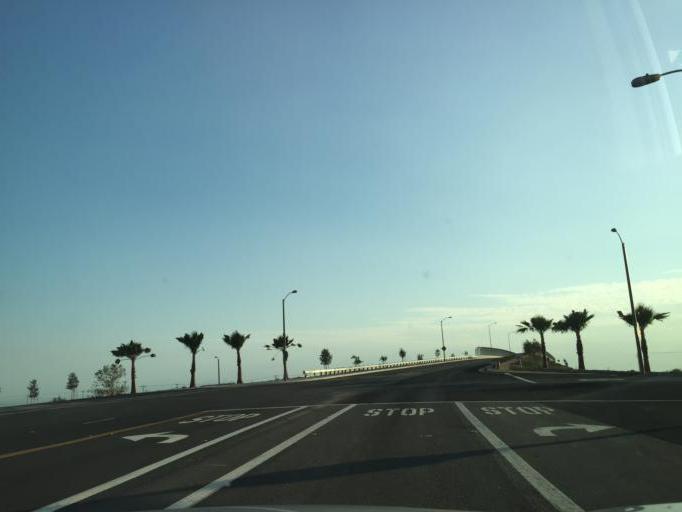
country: US
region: California
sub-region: San Bernardino County
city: Muscoy
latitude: 34.1894
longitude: -117.3625
